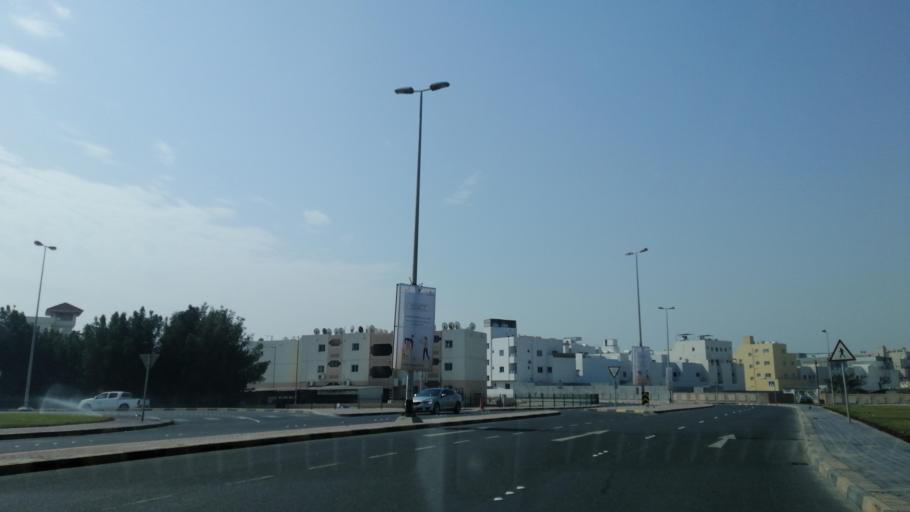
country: BH
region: Muharraq
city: Al Hadd
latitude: 26.2547
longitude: 50.6548
